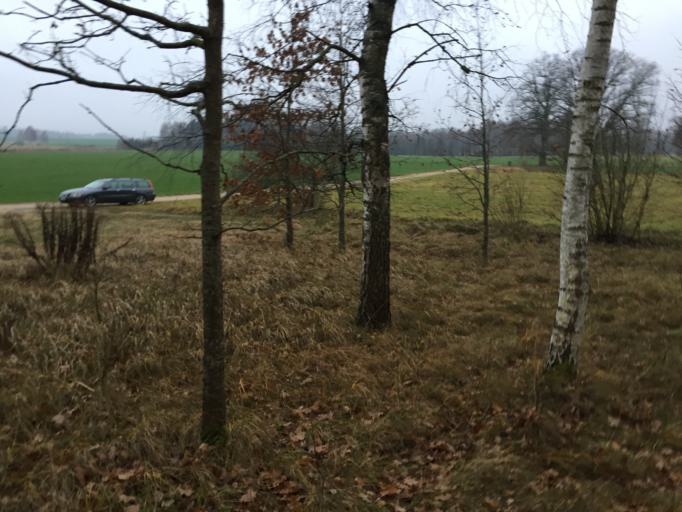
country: LV
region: Koceni
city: Koceni
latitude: 57.5517
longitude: 25.3570
